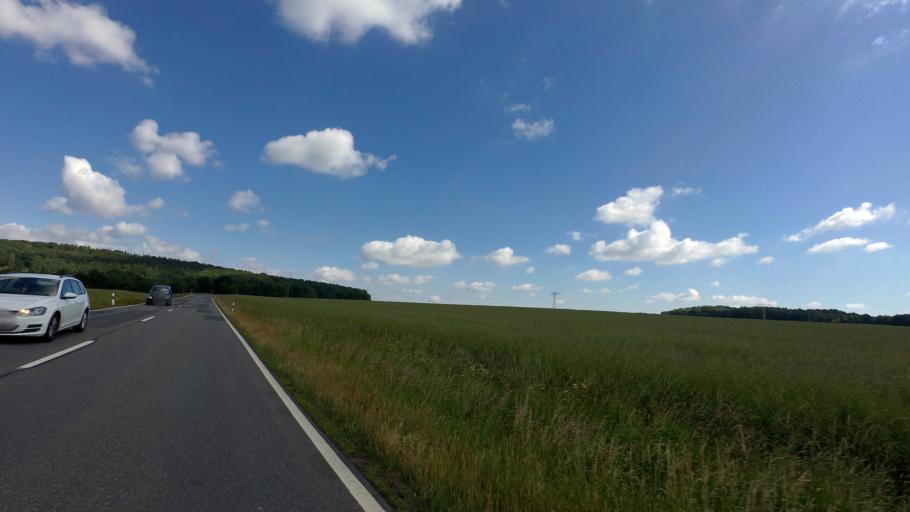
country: DE
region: Saxony
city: Rammenau
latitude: 51.1599
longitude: 14.1436
